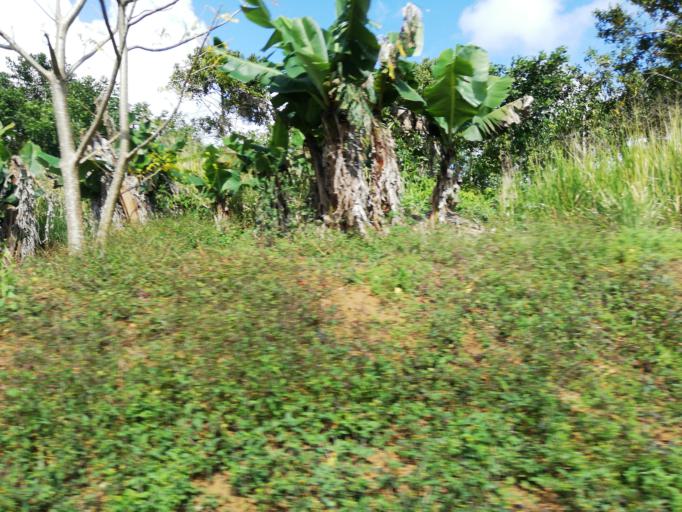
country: MU
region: Pamplemousses
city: Creve Coeur
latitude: -20.2042
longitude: 57.5596
